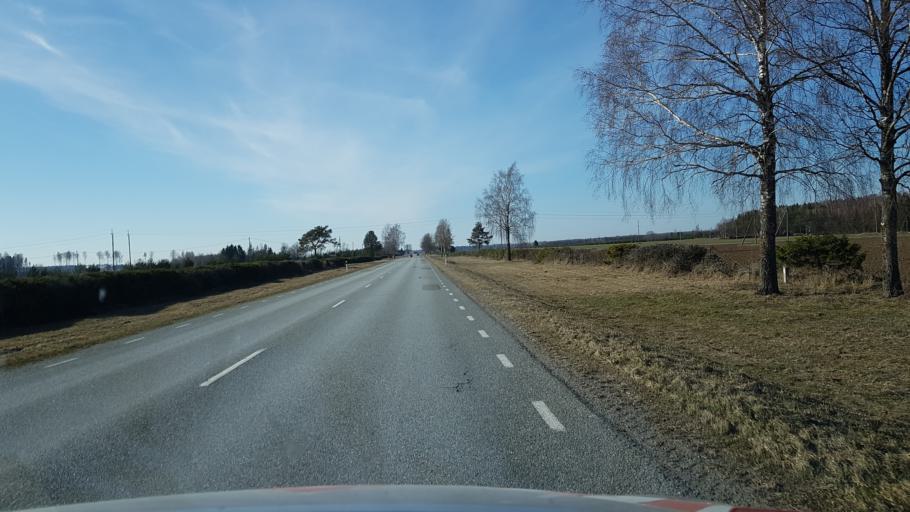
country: EE
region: Laeaene-Virumaa
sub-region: Vinni vald
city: Vinni
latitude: 59.2195
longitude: 26.5350
